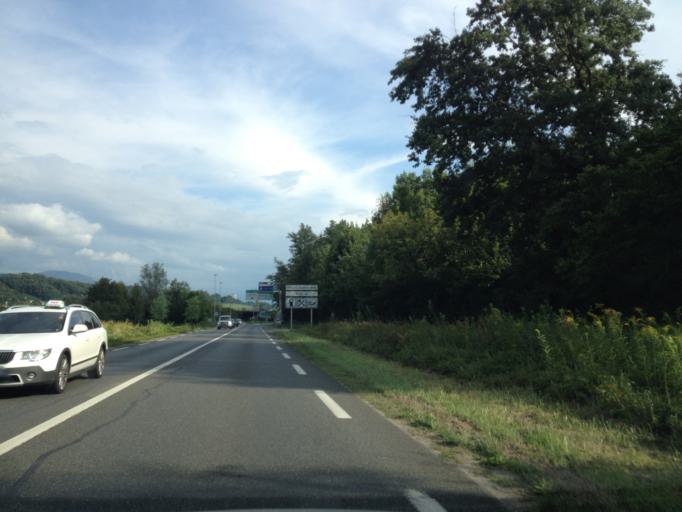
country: FR
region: Rhone-Alpes
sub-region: Departement de la Savoie
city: La Motte-Servolex
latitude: 45.6182
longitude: 5.8814
